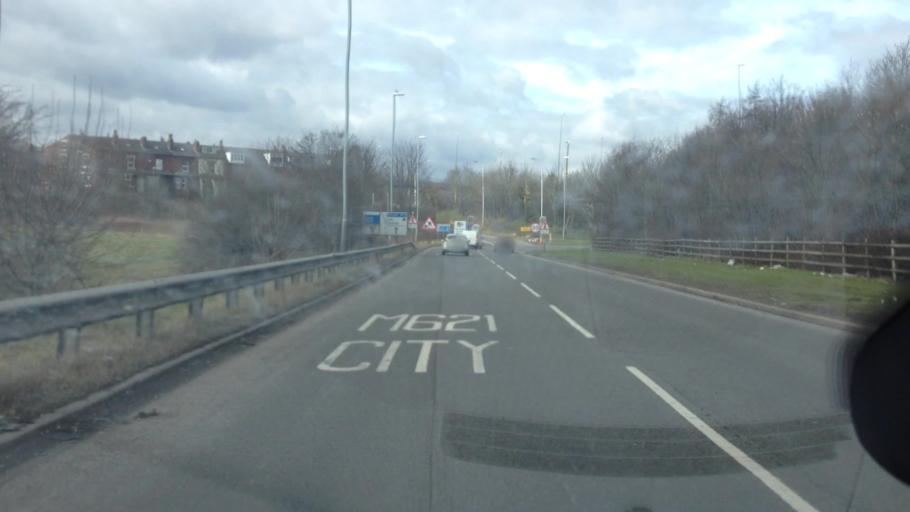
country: GB
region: England
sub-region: City and Borough of Leeds
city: Leeds
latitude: 53.7684
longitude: -1.5169
